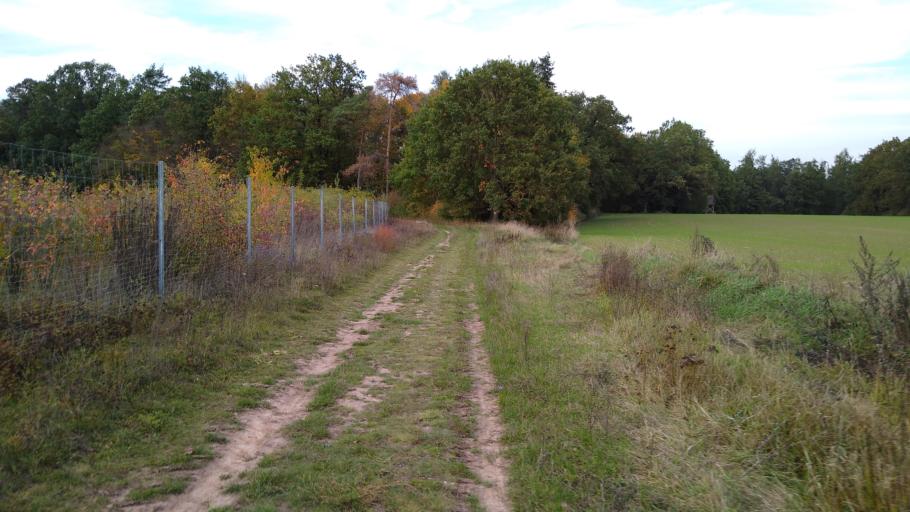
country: DE
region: Bavaria
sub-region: Regierungsbezirk Mittelfranken
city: Obermichelbach
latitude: 49.5023
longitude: 10.9251
